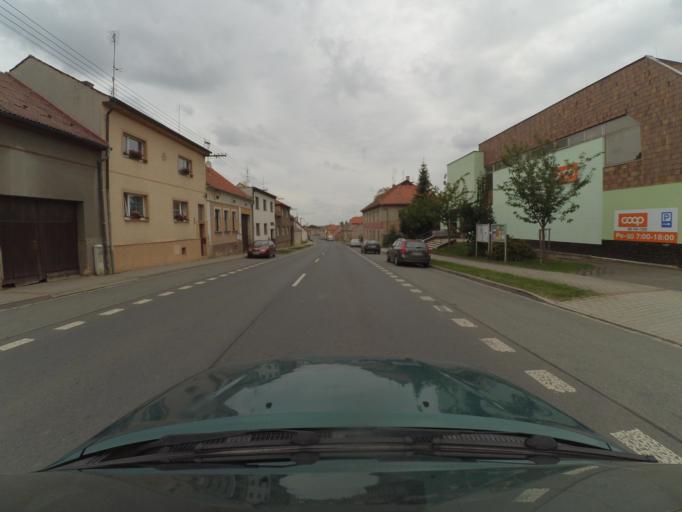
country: CZ
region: Plzensky
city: Kozlany
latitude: 49.9939
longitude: 13.5407
